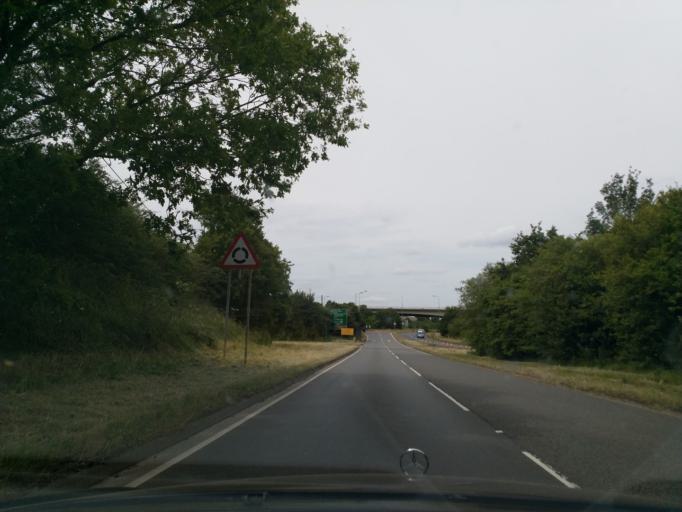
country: GB
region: England
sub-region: Solihull
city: Hampton in Arden
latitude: 52.4433
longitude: -1.6858
